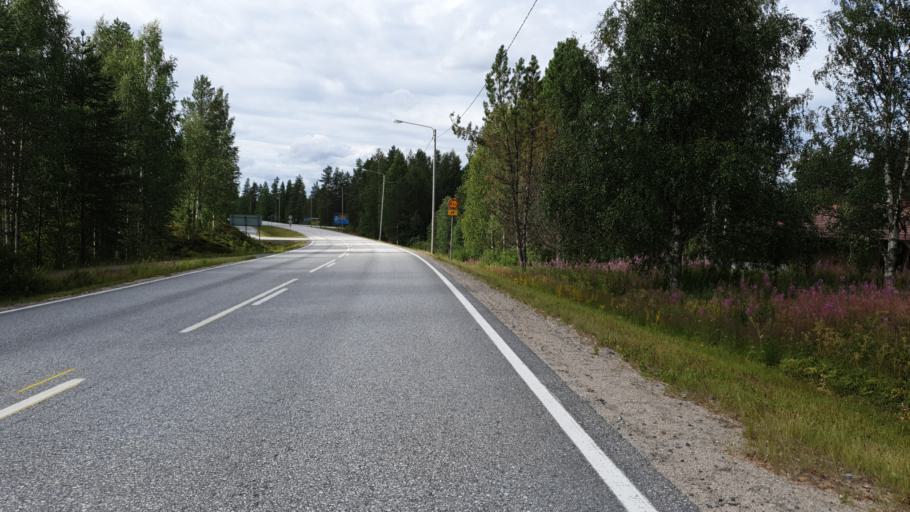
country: FI
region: Kainuu
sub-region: Kehys-Kainuu
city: Kuhmo
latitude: 64.5390
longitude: 29.9485
